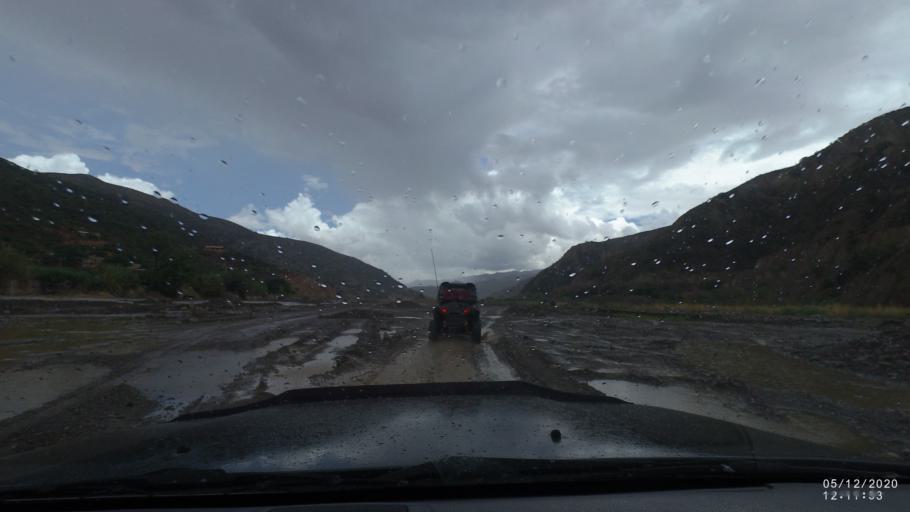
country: BO
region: Cochabamba
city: Sipe Sipe
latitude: -17.5649
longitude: -66.3746
